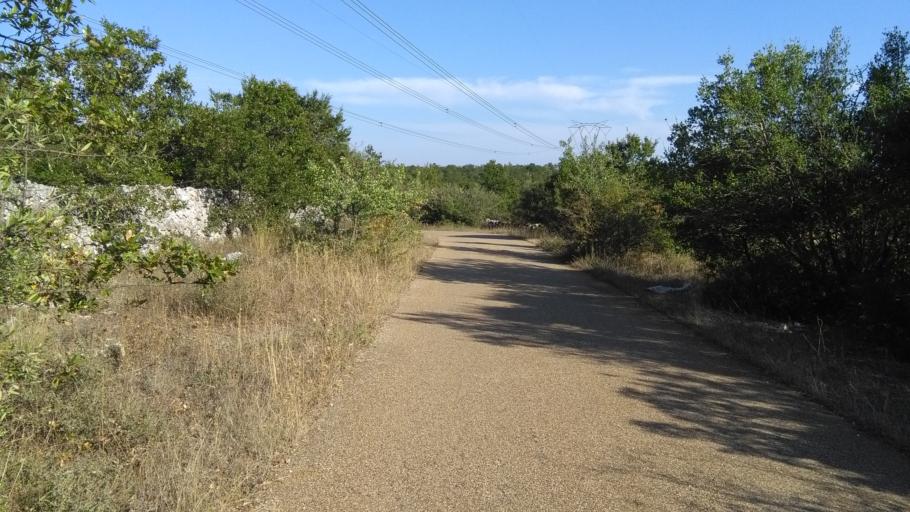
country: IT
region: Apulia
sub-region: Provincia di Bari
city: Putignano
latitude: 40.8181
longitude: 17.0562
